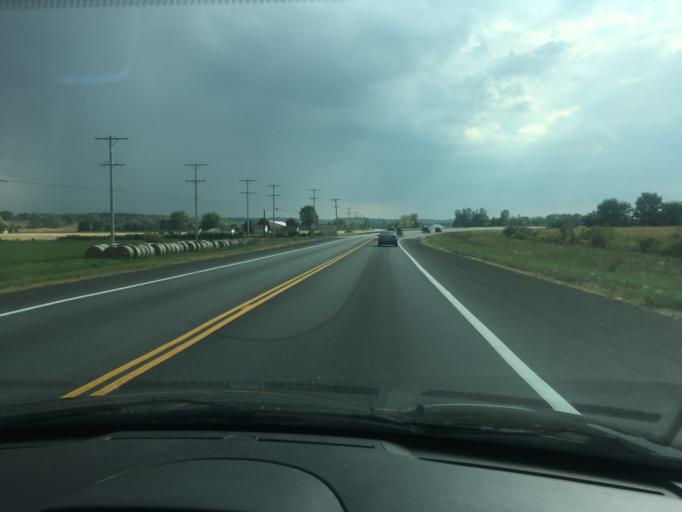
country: US
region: Ohio
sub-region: Clark County
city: Northridge
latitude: 40.0440
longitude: -83.7797
